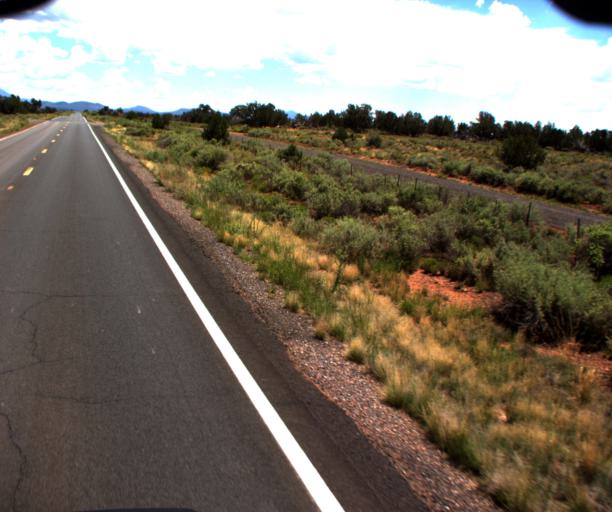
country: US
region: Arizona
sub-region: Coconino County
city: Williams
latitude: 35.6440
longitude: -112.1303
